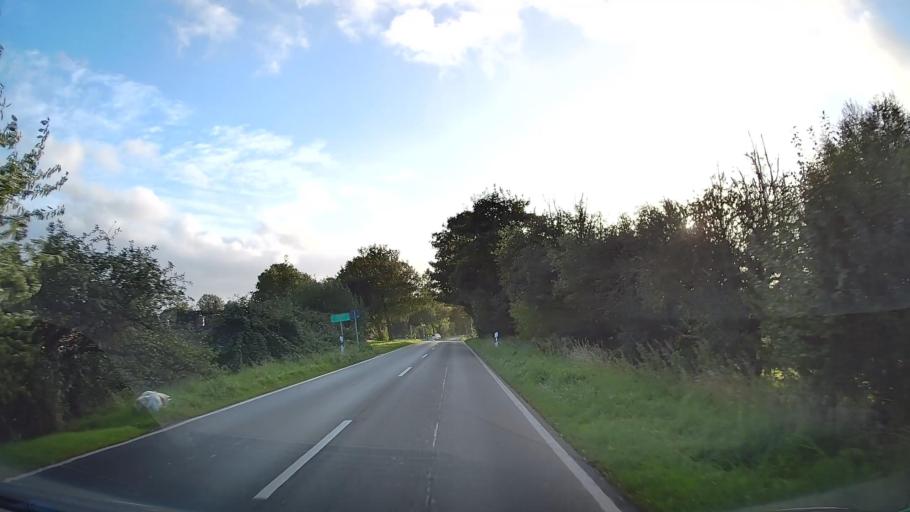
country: DE
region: Schleswig-Holstein
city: Herzhorn
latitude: 53.7897
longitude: 9.4844
